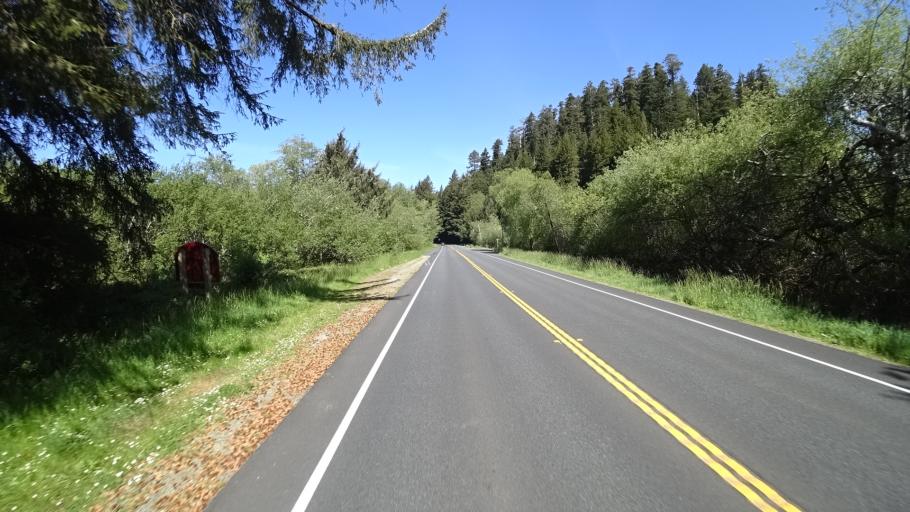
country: US
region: California
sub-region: Del Norte County
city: Bertsch-Oceanview
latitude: 41.5609
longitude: -124.0620
